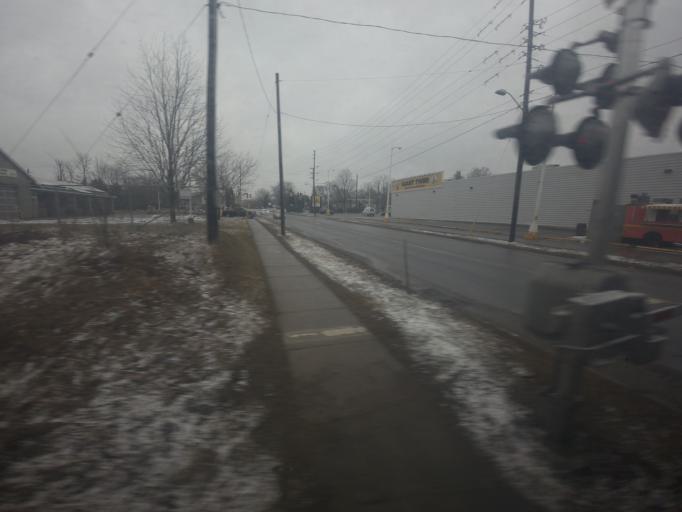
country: CA
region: Ontario
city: Brockville
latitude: 44.6011
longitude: -75.6914
